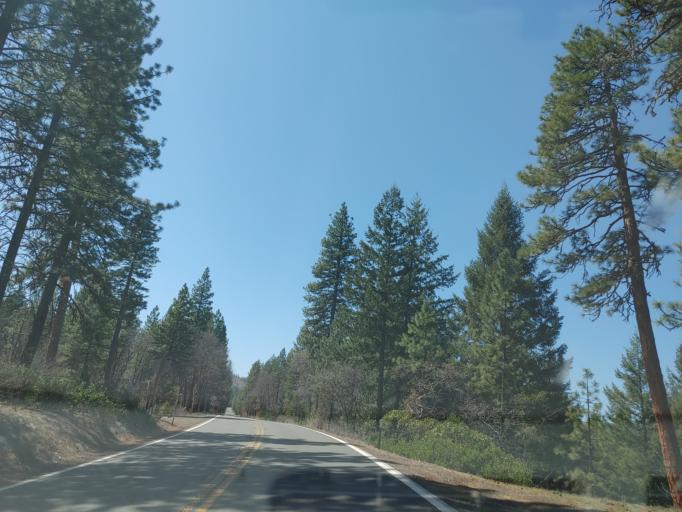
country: US
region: California
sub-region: Shasta County
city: Burney
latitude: 41.0167
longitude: -121.6315
